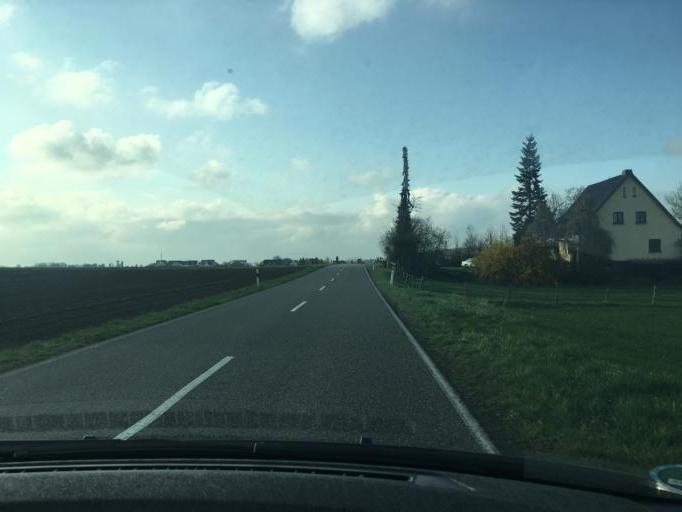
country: DE
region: North Rhine-Westphalia
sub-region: Regierungsbezirk Koln
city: Weilerswist
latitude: 50.7273
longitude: 6.9000
